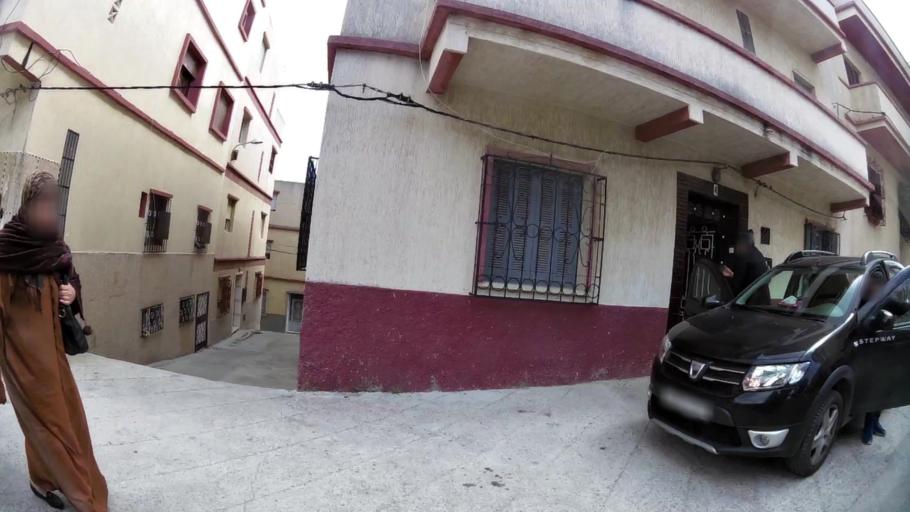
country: MA
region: Tanger-Tetouan
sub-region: Tanger-Assilah
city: Tangier
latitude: 35.7591
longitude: -5.8164
